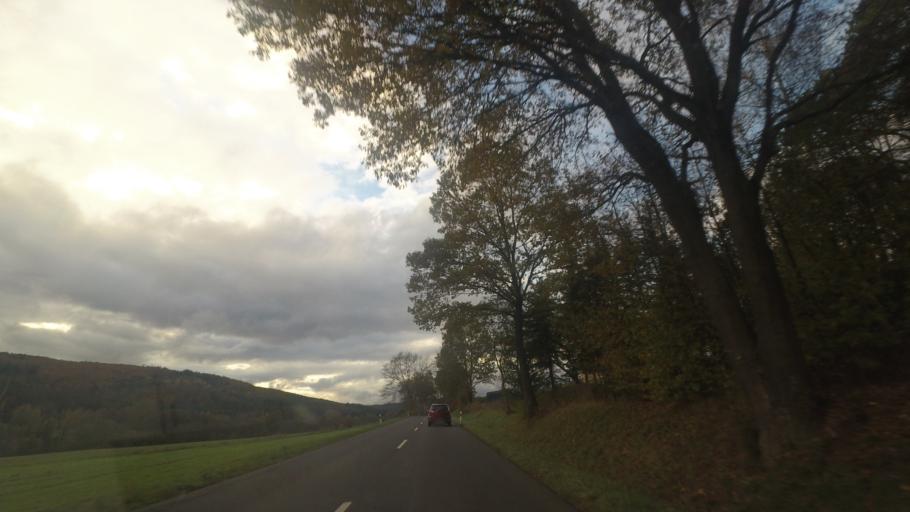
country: DE
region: Hesse
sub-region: Regierungsbezirk Kassel
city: Flieden
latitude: 50.4548
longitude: 9.5562
